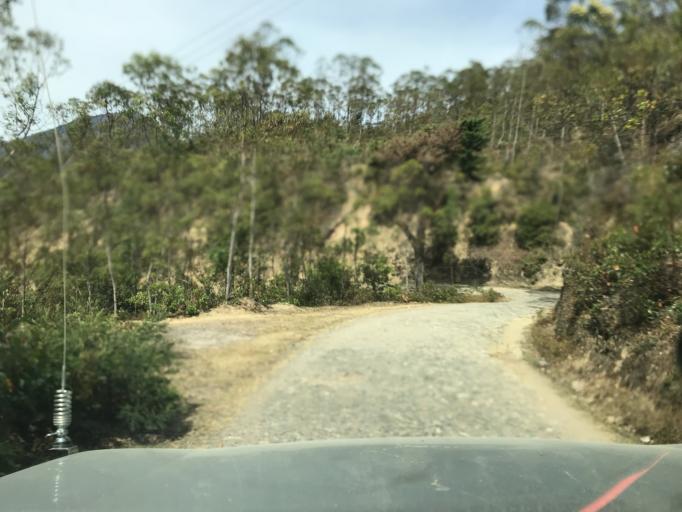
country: TL
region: Ainaro
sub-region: Ainaro
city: Ainaro
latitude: -8.8837
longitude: 125.5265
